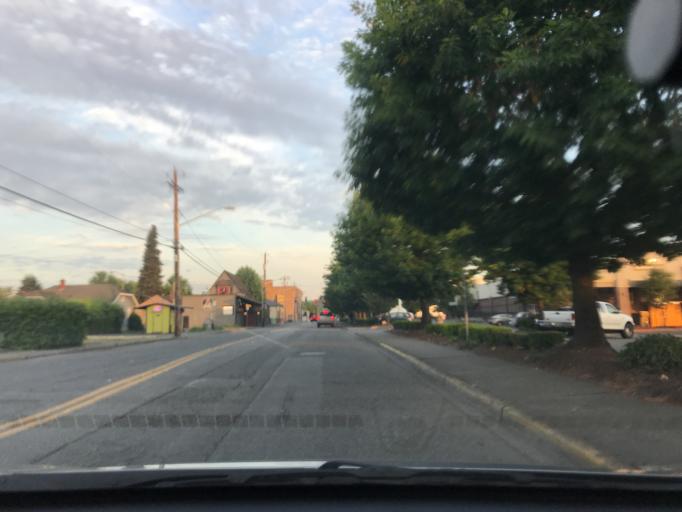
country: US
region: Washington
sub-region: King County
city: Auburn
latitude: 47.3057
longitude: -122.2261
